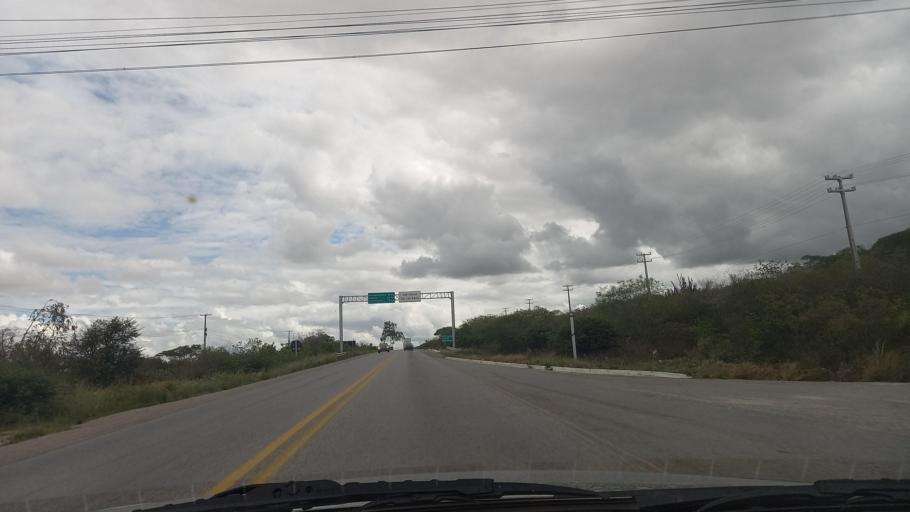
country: BR
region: Pernambuco
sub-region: Cachoeirinha
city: Cachoeirinha
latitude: -8.3321
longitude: -36.1496
